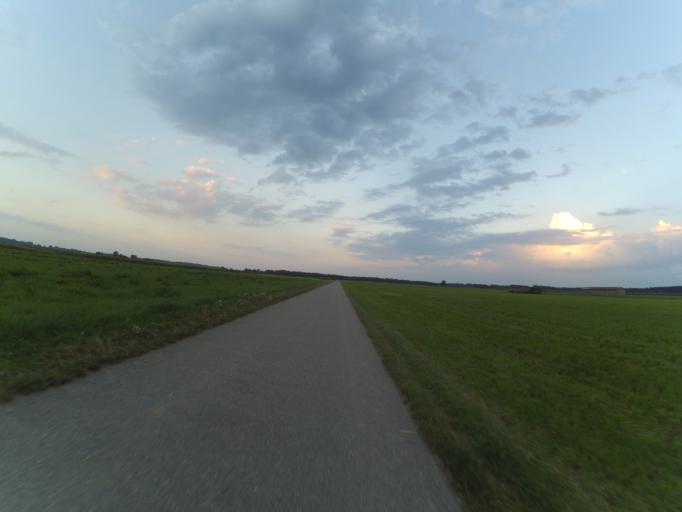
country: DE
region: Bavaria
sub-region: Swabia
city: Turkheim
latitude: 48.0559
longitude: 10.5961
